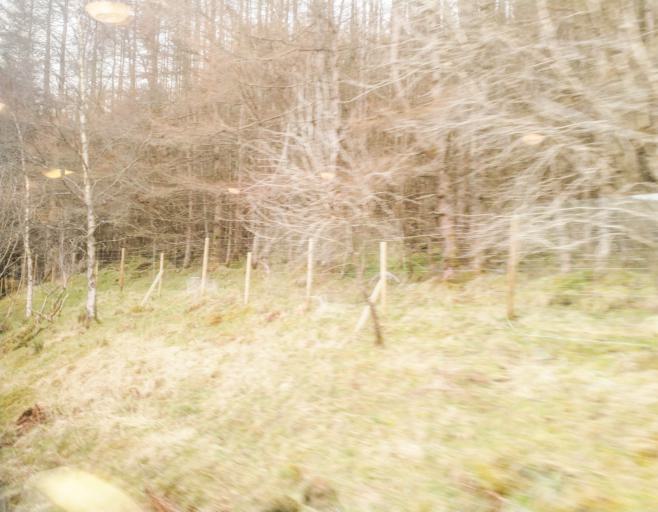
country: GB
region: Scotland
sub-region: Argyll and Bute
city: Garelochhead
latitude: 56.4438
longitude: -4.7080
